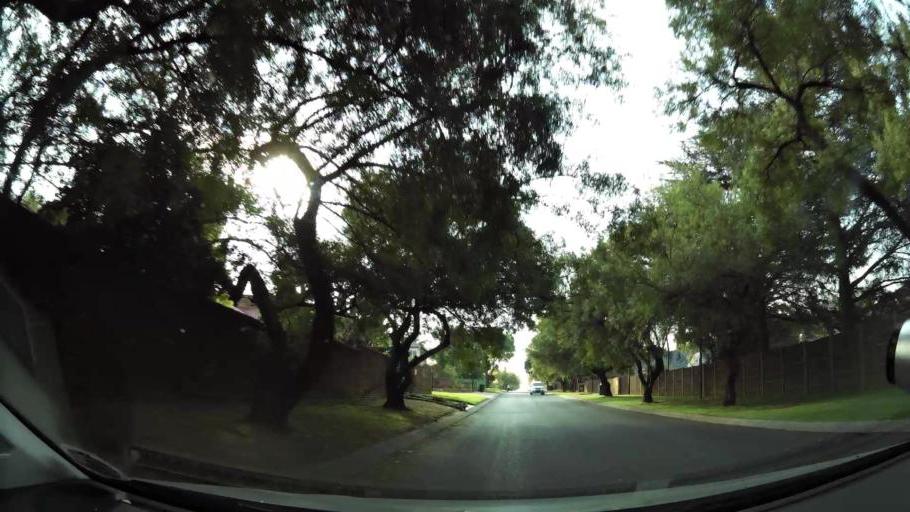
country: ZA
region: Gauteng
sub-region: City of Johannesburg Metropolitan Municipality
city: Modderfontein
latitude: -26.0823
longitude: 28.2023
